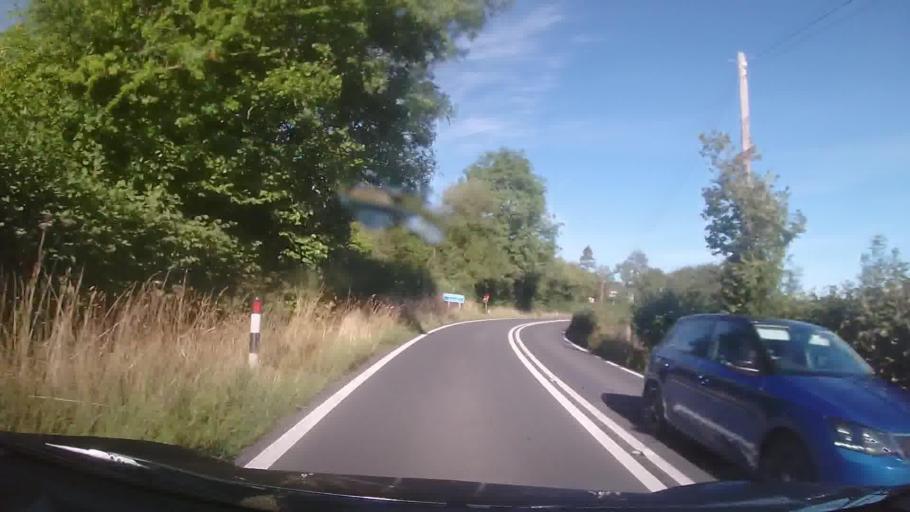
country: GB
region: Wales
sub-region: Sir Powys
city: Hay
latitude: 51.9566
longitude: -3.2012
